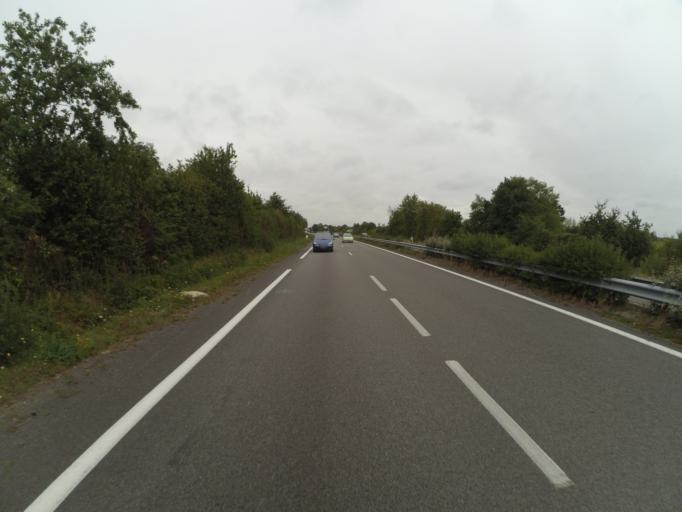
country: FR
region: Pays de la Loire
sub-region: Departement de la Vendee
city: Belleville-sur-Vie
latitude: 46.7856
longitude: -1.4215
